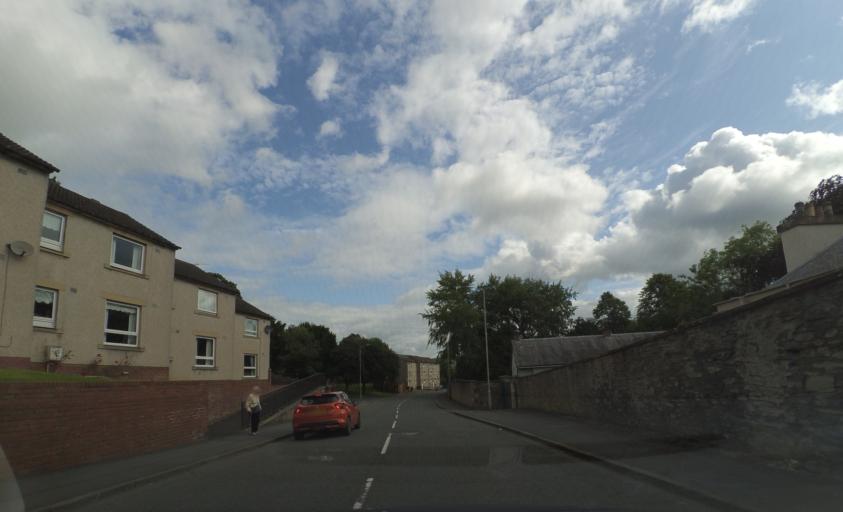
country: GB
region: Scotland
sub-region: The Scottish Borders
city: Hawick
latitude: 55.4264
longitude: -2.7899
